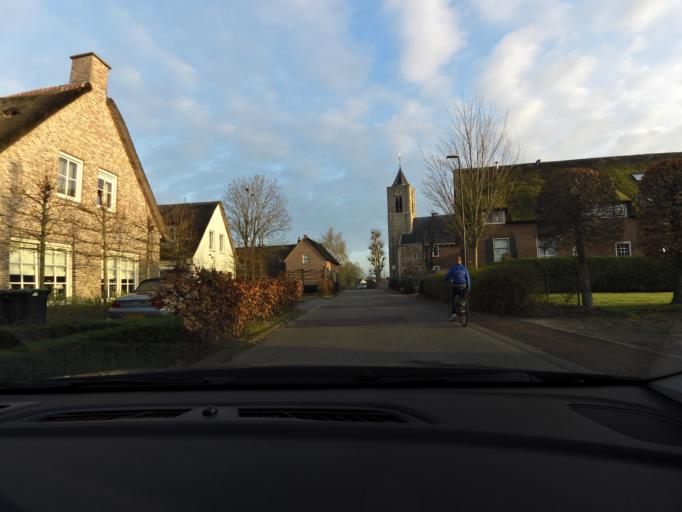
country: NL
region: South Holland
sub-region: Gemeente Gorinchem
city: Gorinchem
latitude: 51.8795
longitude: 4.9469
